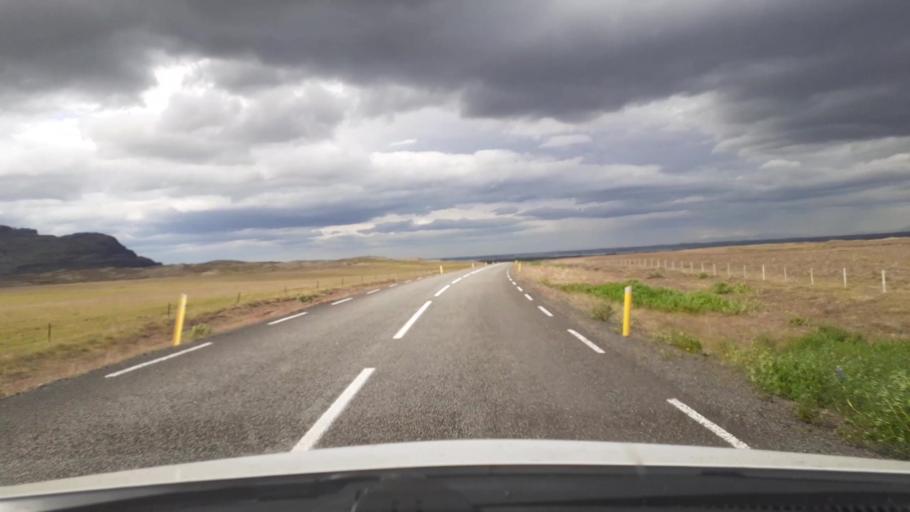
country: IS
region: West
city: Borgarnes
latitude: 64.5445
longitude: -21.6656
